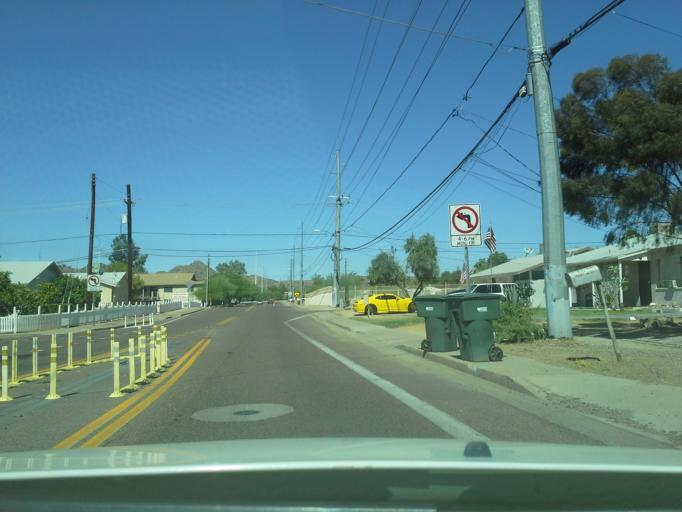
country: US
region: Arizona
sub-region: Maricopa County
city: Paradise Valley
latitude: 33.5726
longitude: -112.0567
